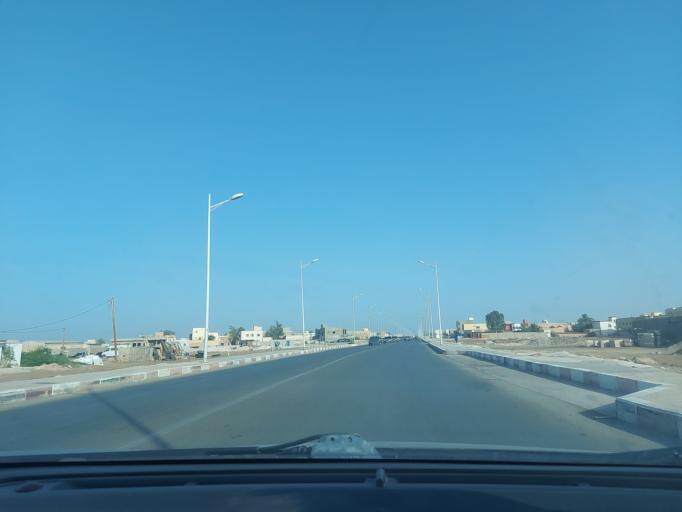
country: MR
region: Nouakchott
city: Nouakchott
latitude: 18.0854
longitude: -16.0012
